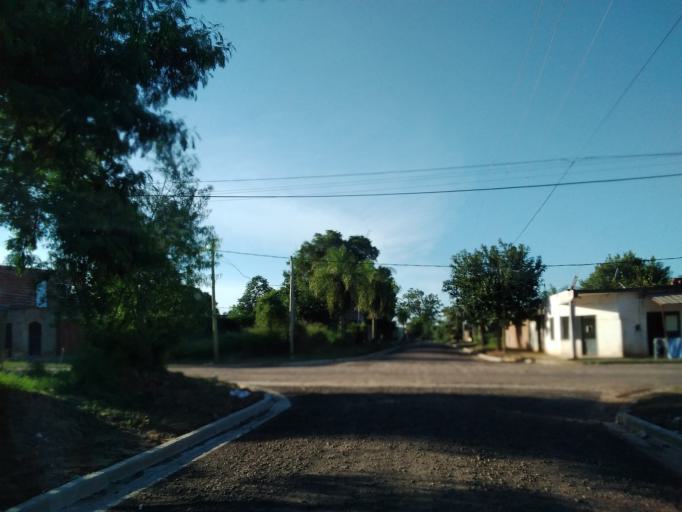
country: AR
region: Corrientes
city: Corrientes
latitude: -27.5061
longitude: -58.7992
